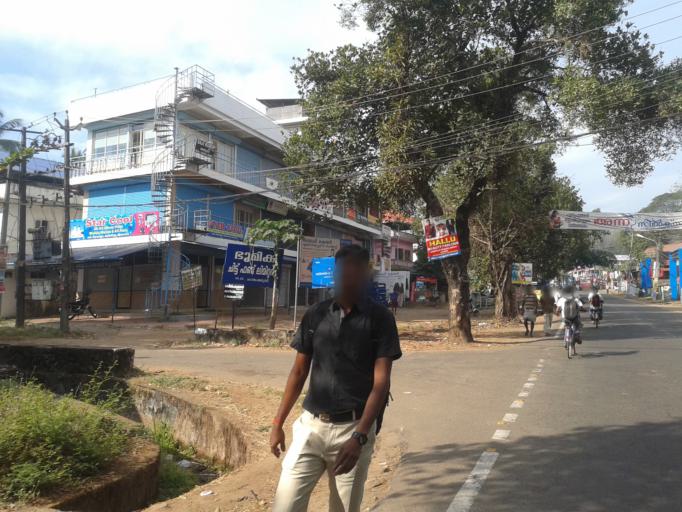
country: IN
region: Kerala
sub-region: Thrissur District
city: Kizhake Chalakudi
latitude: 10.3076
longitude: 76.3359
